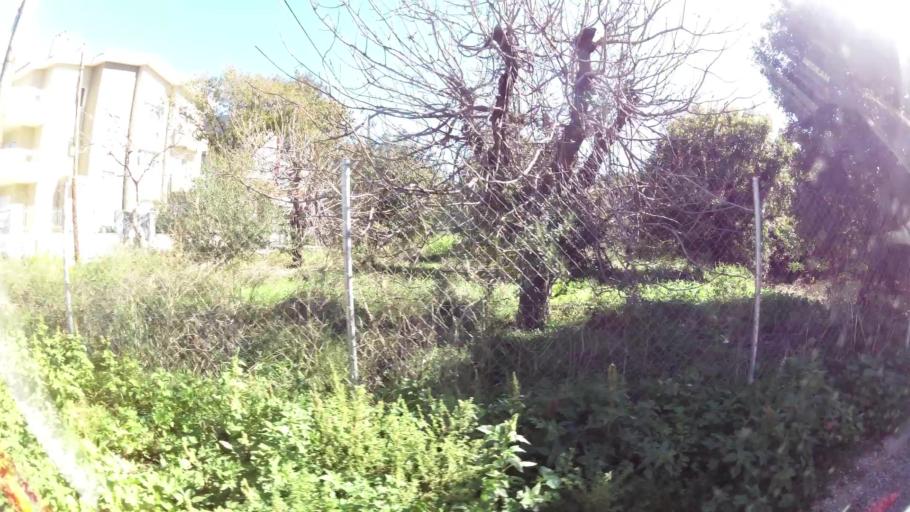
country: GR
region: Attica
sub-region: Nomarchia Anatolikis Attikis
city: Leondarion
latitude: 37.9982
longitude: 23.8601
